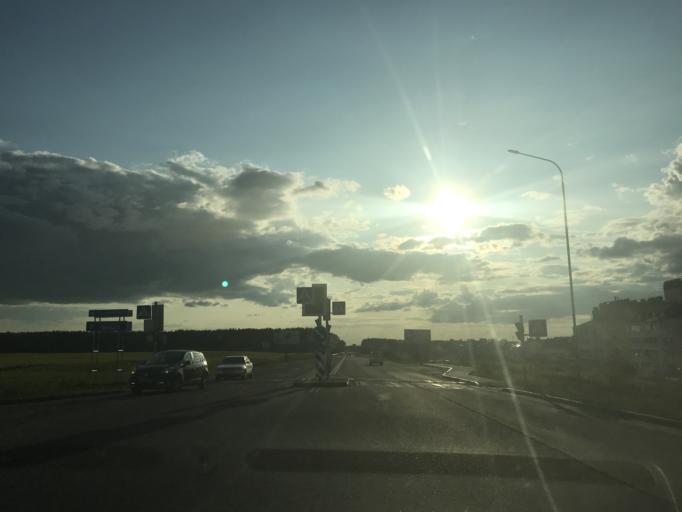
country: BY
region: Minsk
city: Borovlyany
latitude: 53.9685
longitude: 27.6233
